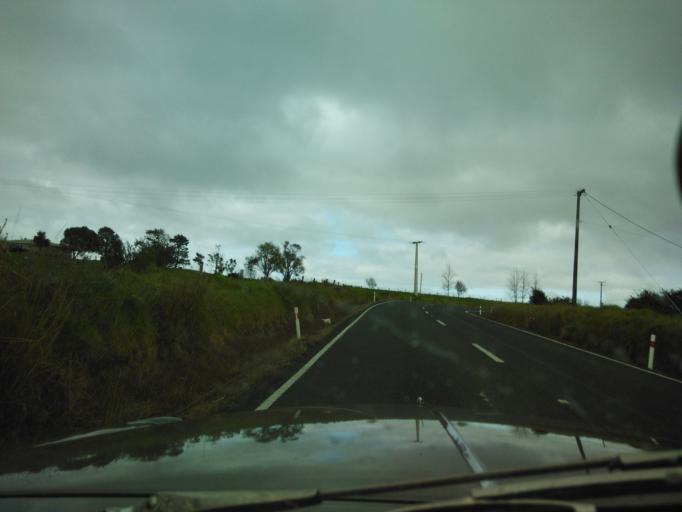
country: NZ
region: Auckland
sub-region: Auckland
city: Wellsford
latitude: -36.1405
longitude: 174.5058
